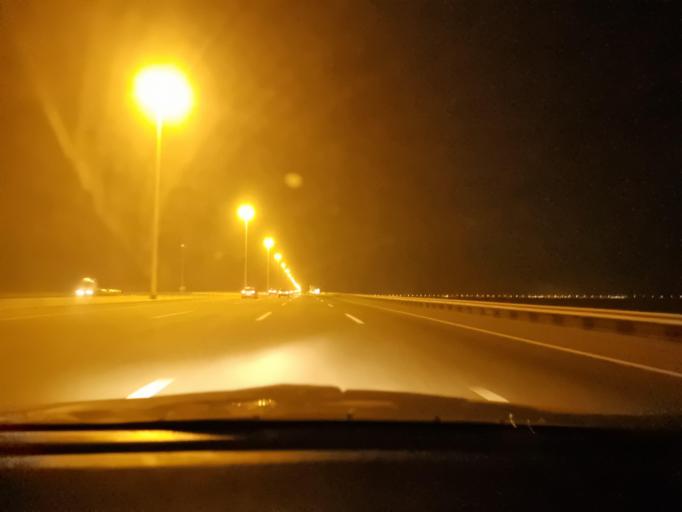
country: AE
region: Dubai
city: Dubai
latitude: 24.7508
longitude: 54.9221
